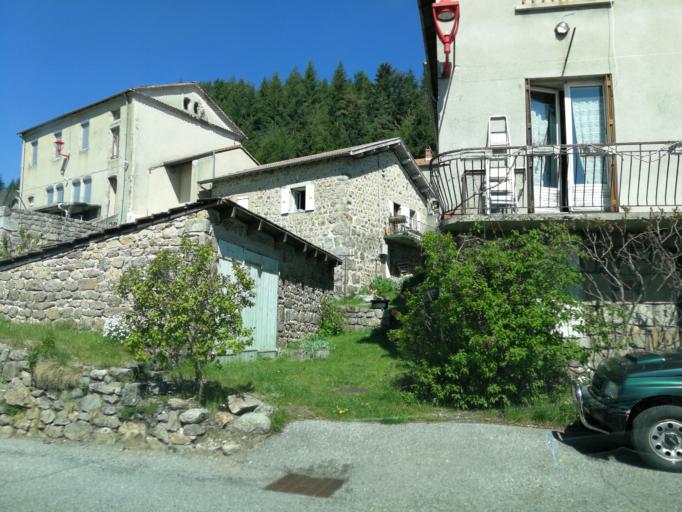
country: FR
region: Rhone-Alpes
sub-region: Departement de l'Ardeche
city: Le Cheylard
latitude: 44.9419
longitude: 4.4294
